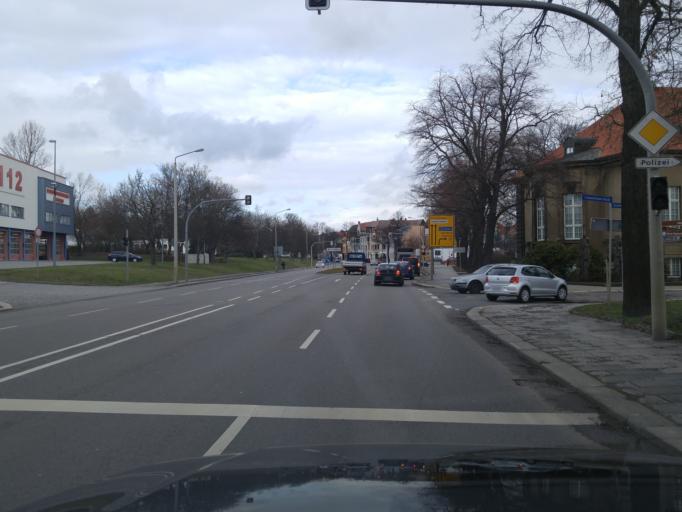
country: DE
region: Saxony
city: Zwickau
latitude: 50.7241
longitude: 12.4863
